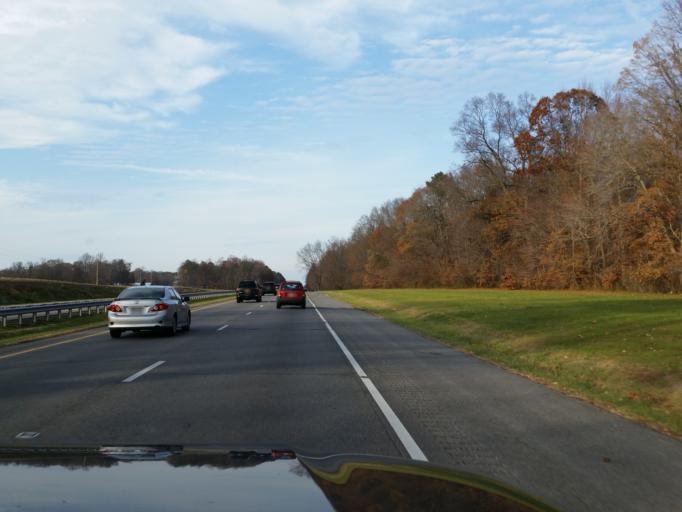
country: US
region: Maryland
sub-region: Talbot County
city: Easton
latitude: 38.8551
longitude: -76.0607
